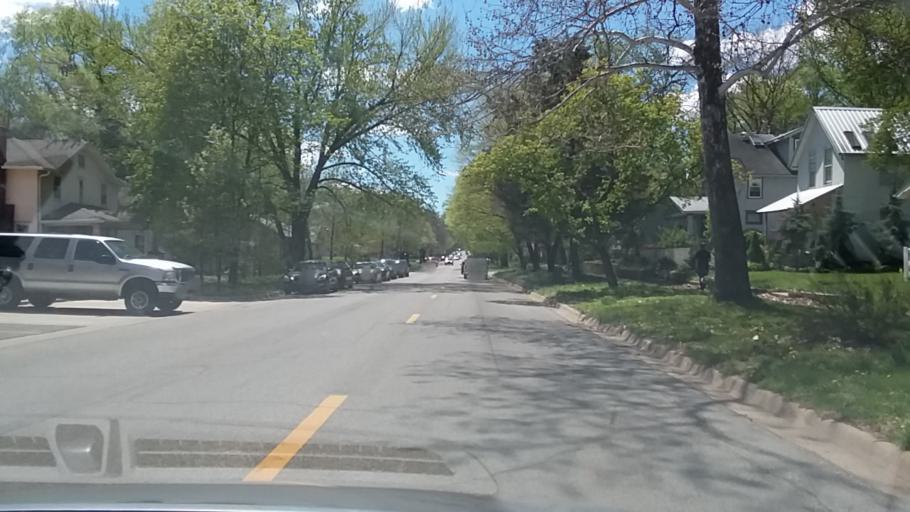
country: US
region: Kansas
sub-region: Douglas County
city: Lawrence
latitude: 38.9703
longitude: -95.2324
